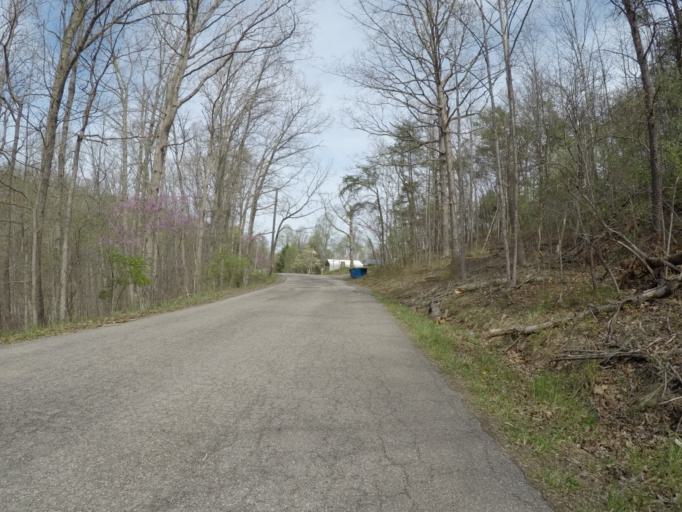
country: US
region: West Virginia
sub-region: Wayne County
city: Lavalette
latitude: 38.3515
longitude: -82.3990
